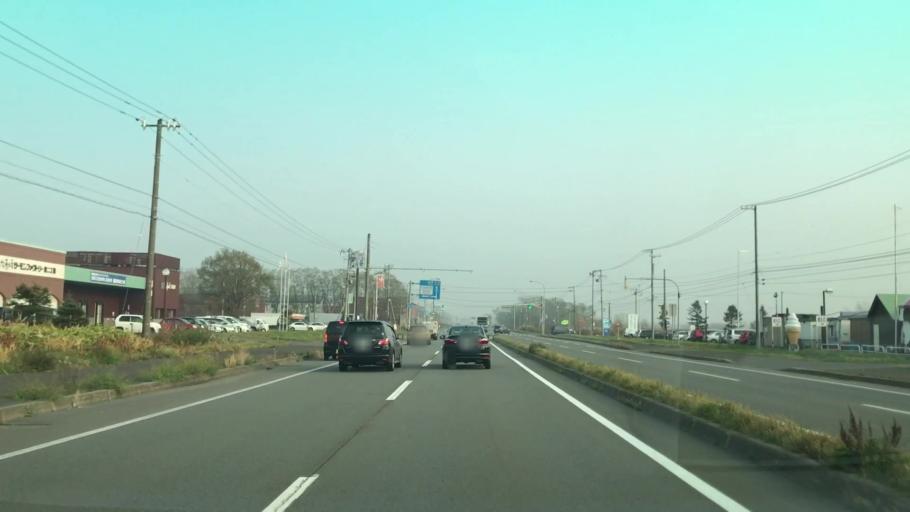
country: JP
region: Hokkaido
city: Ishikari
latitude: 43.2068
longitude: 141.3325
